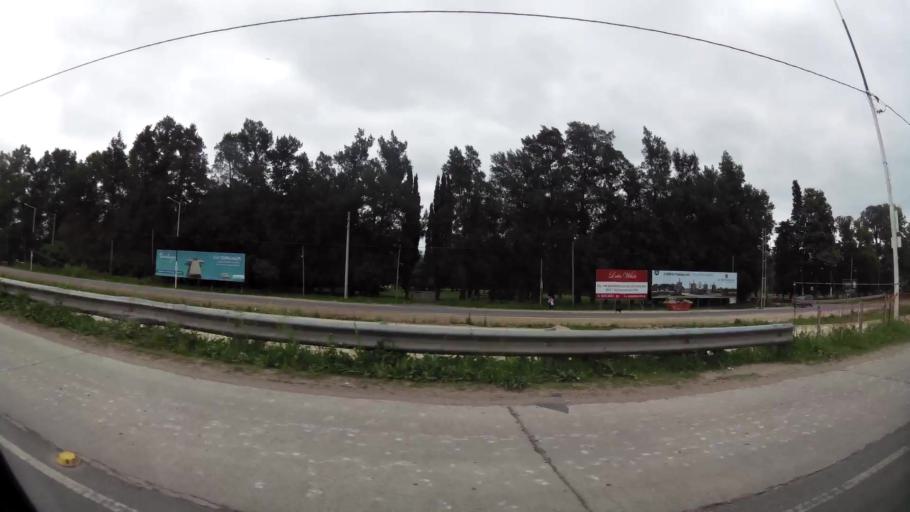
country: AR
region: Buenos Aires
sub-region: Partido de Ezeiza
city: Ezeiza
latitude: -34.8985
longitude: -58.5091
